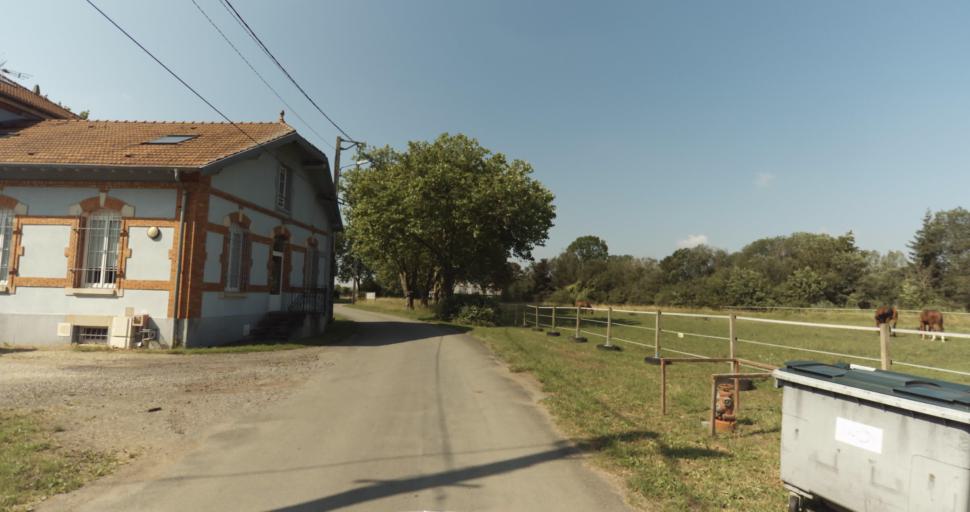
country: FR
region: Lorraine
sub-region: Departement de Meurthe-et-Moselle
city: Mancieulles
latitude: 49.2822
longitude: 5.9065
